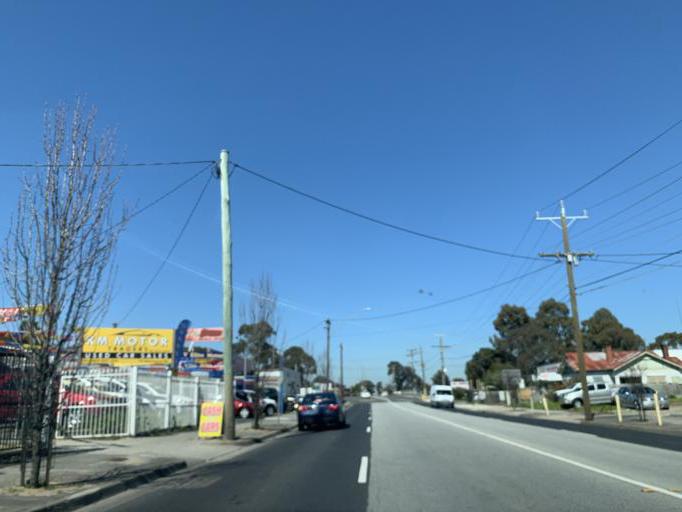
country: AU
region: Victoria
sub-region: Greater Dandenong
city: Dandenong
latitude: -37.9922
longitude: 145.2101
